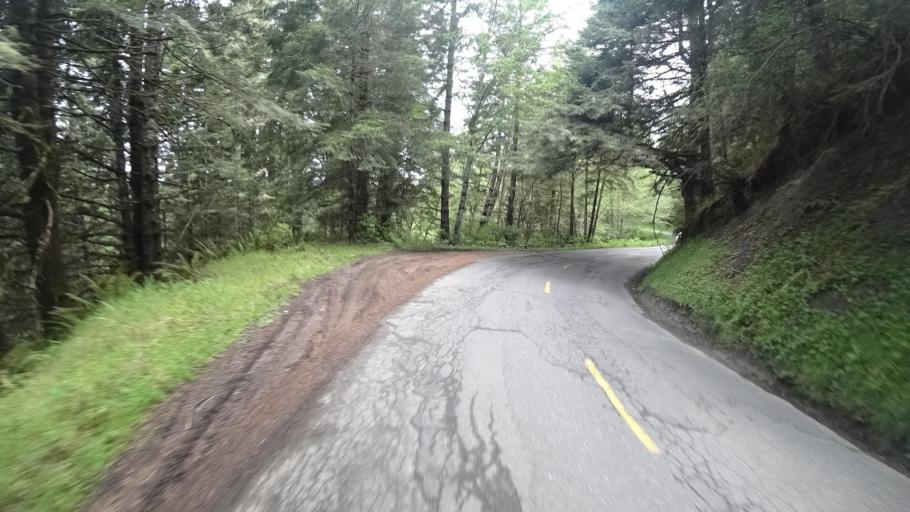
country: US
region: California
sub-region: Humboldt County
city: Ferndale
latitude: 40.5259
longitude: -124.2677
